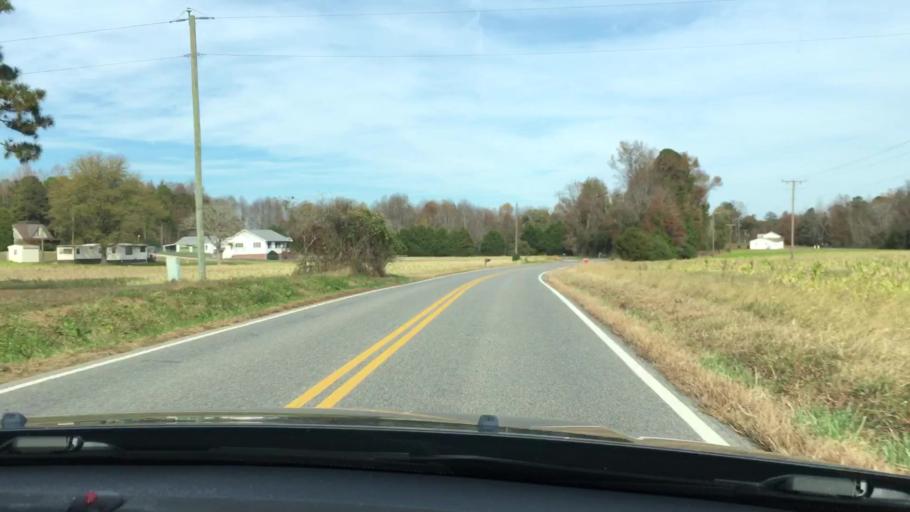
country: US
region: Virginia
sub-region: King William County
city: West Point
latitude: 37.4827
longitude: -76.8164
